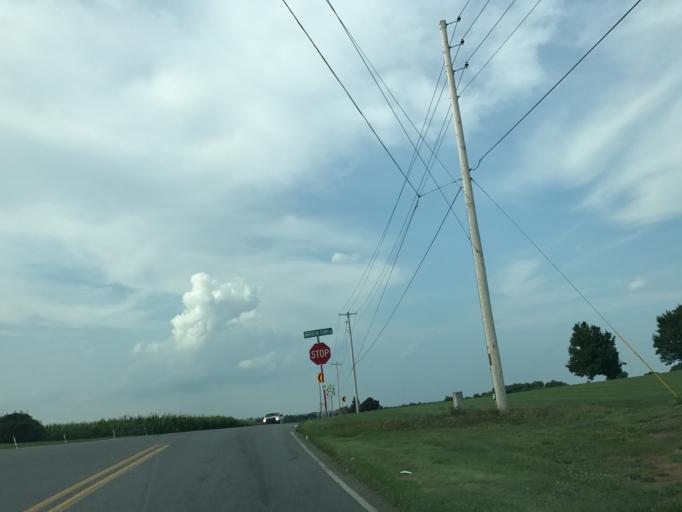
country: US
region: Pennsylvania
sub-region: Lancaster County
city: Marietta
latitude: 40.0732
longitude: -76.5392
